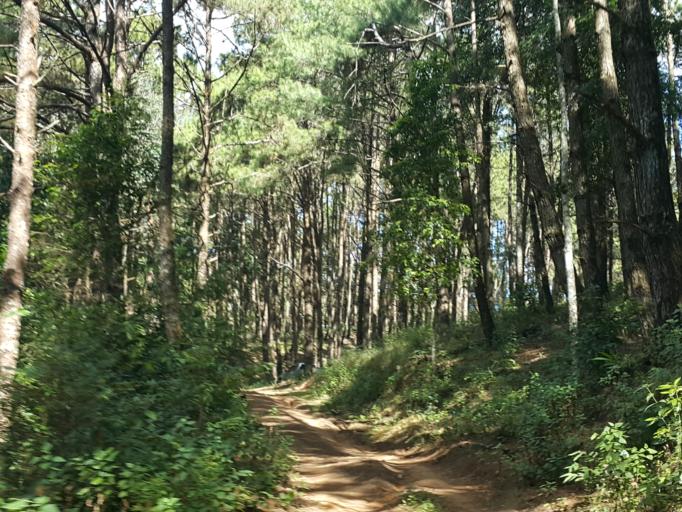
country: TH
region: Chiang Mai
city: Wiang Haeng
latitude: 19.5426
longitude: 98.8152
